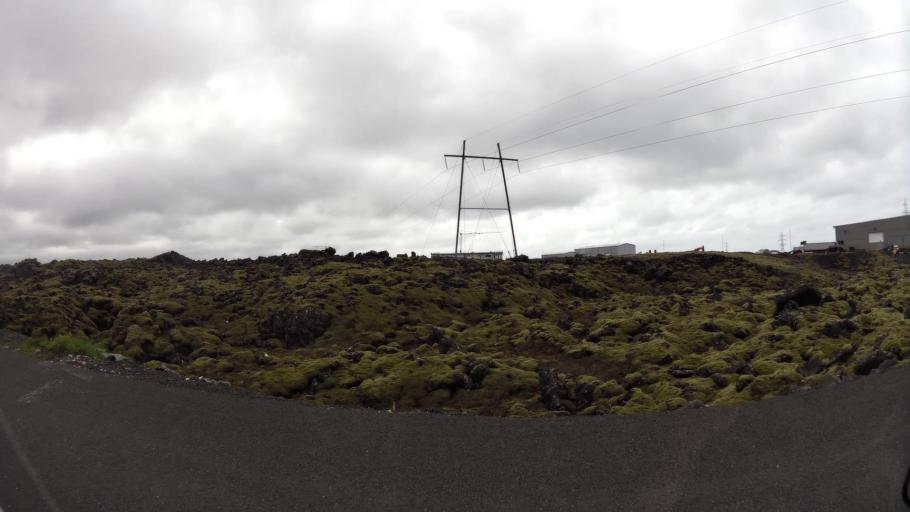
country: IS
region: Capital Region
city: Hafnarfjoerdur
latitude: 64.0380
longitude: -21.9861
